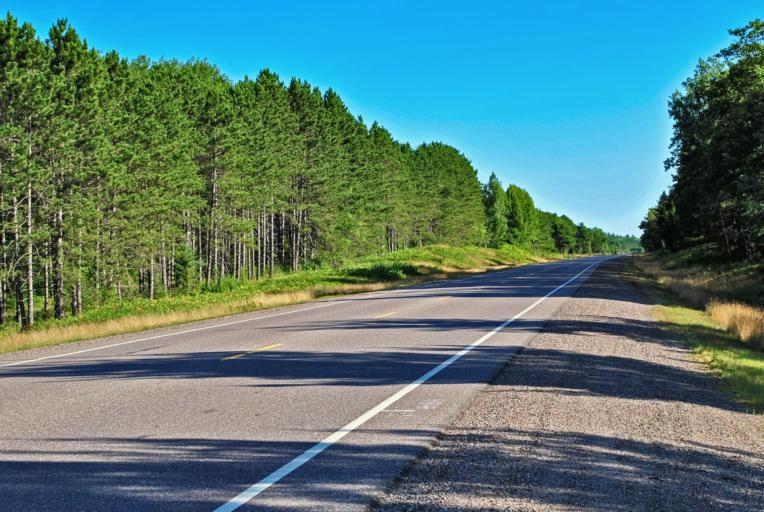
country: US
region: Wisconsin
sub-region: Vilas County
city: Lac du Flambeau
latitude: 45.9664
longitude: -89.6999
